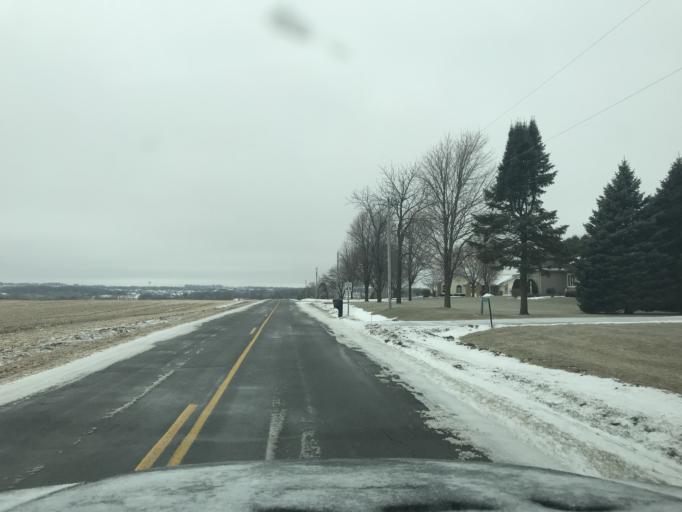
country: US
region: Wisconsin
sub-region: Dane County
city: Cottage Grove
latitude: 43.1043
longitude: -89.2303
